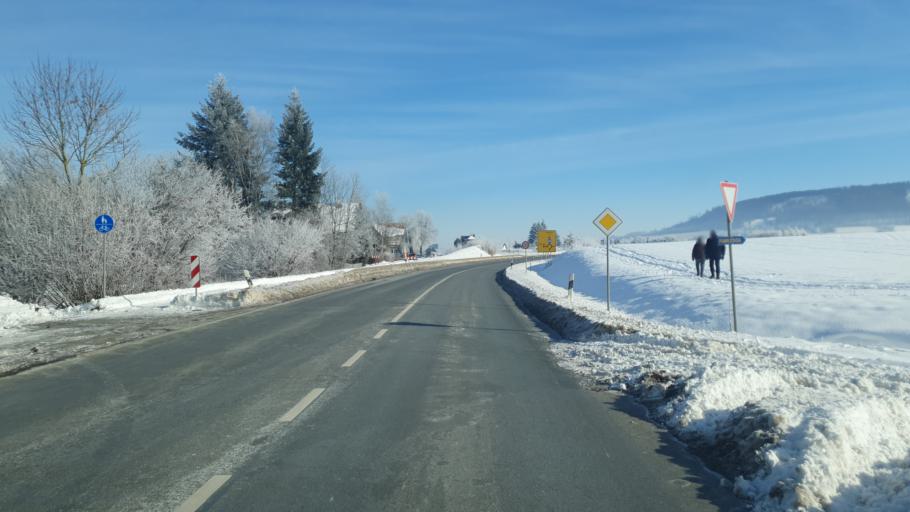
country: DE
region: Lower Saxony
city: Aerzen
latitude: 52.0341
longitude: 9.2445
